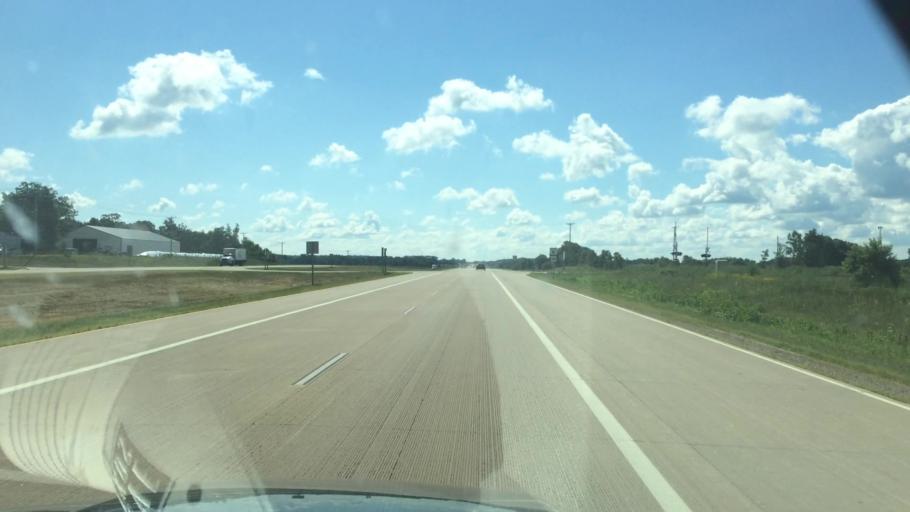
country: US
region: Wisconsin
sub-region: Portage County
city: Amherst
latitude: 44.4947
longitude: -89.3675
